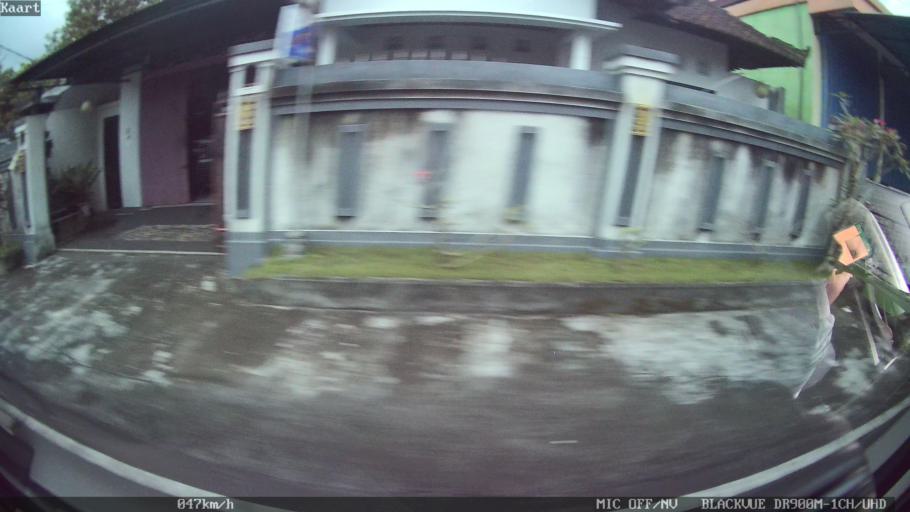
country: ID
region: Bali
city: Banjar Serangan
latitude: -8.5524
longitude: 115.1810
